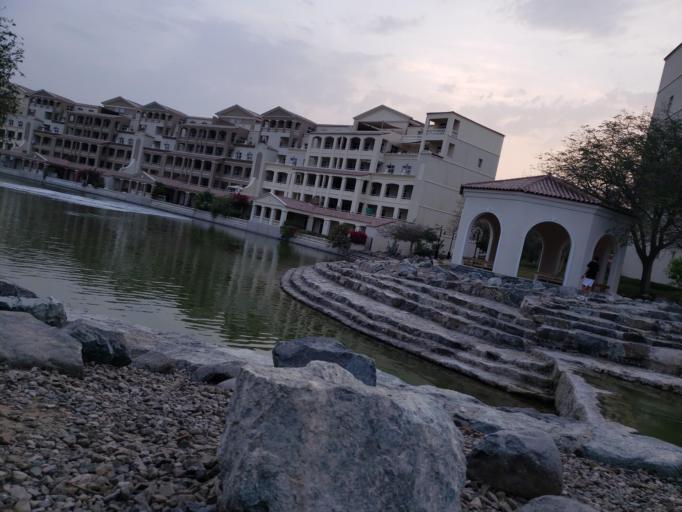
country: AE
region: Dubai
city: Dubai
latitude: 25.0410
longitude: 55.2315
